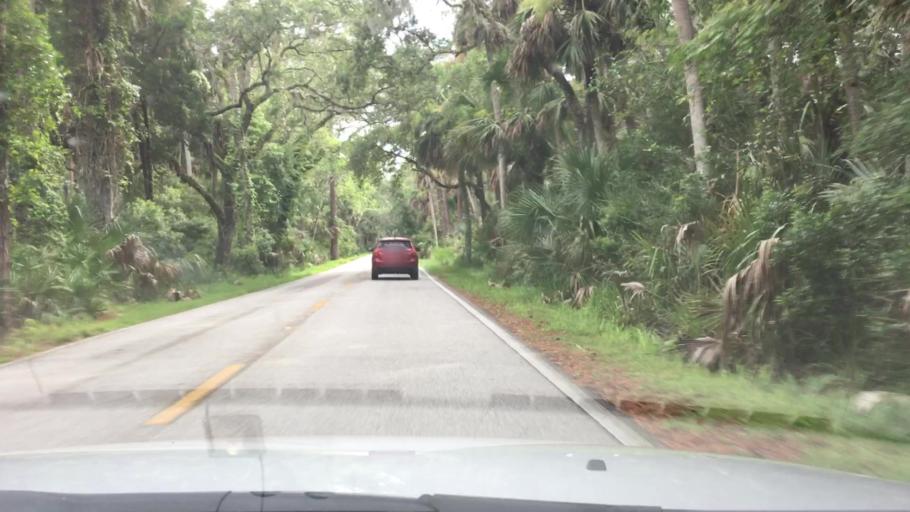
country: US
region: Florida
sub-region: Volusia County
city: Ormond-by-the-Sea
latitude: 29.3413
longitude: -81.1002
